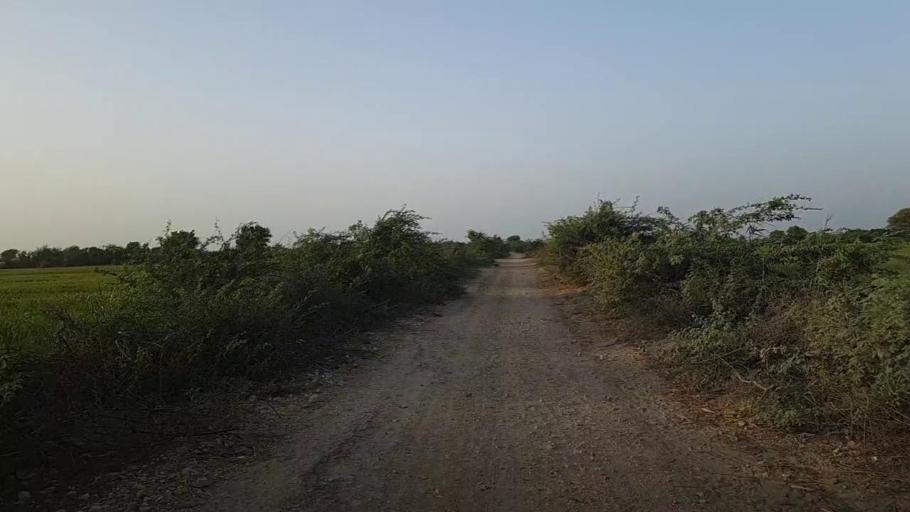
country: PK
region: Sindh
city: Kario
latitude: 24.7114
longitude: 68.4620
